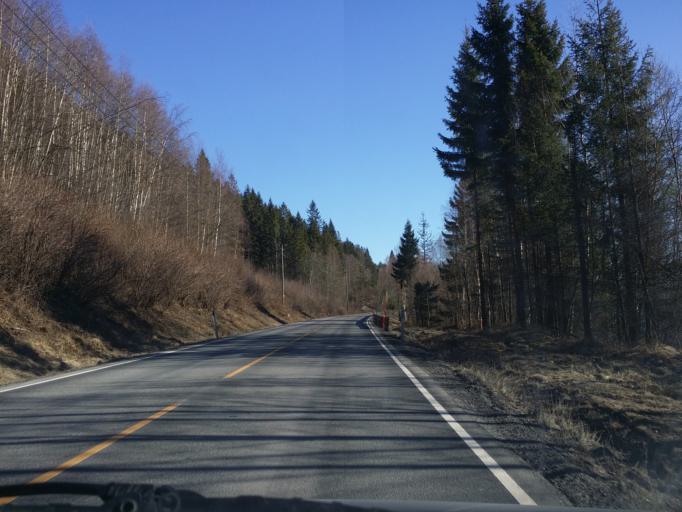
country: NO
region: Buskerud
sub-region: Ringerike
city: Honefoss
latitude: 60.3310
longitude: 10.1219
